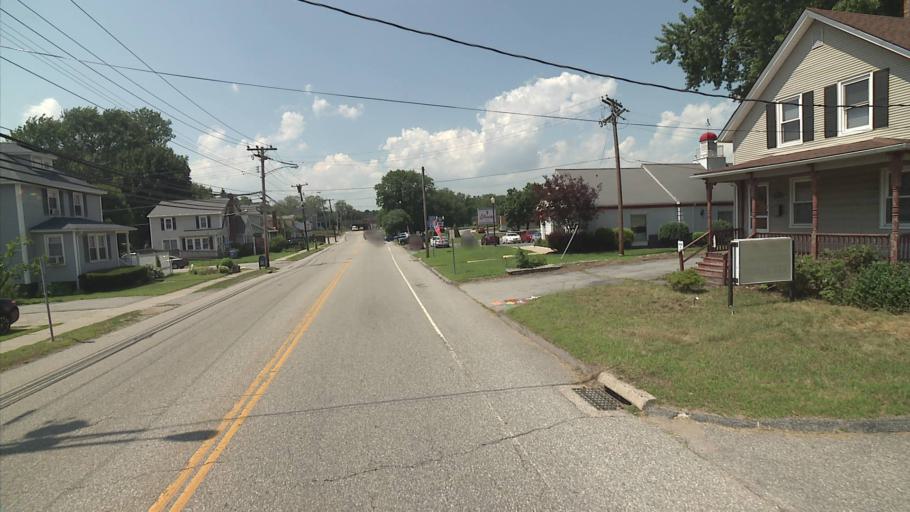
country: US
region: Connecticut
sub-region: New London County
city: Norwich
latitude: 41.5517
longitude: -72.1029
